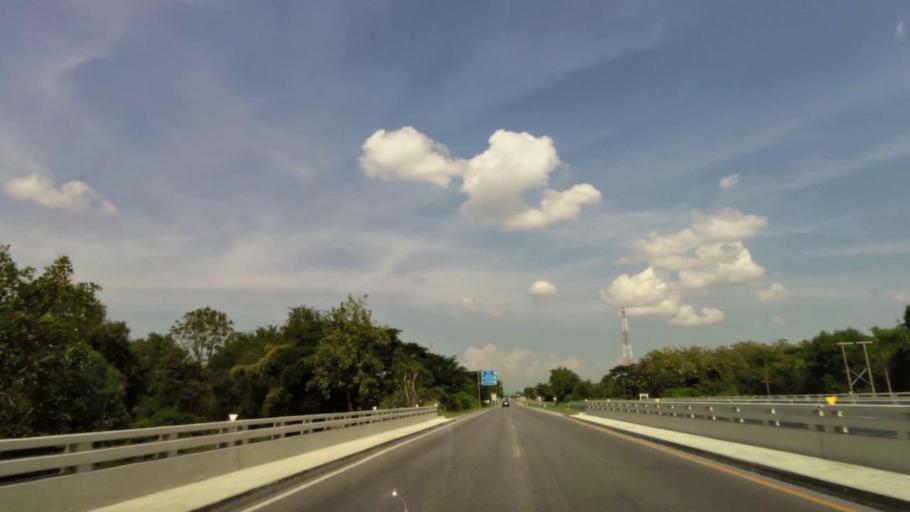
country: TH
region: Uttaradit
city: Thong Saen Khan
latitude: 17.4644
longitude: 100.2371
